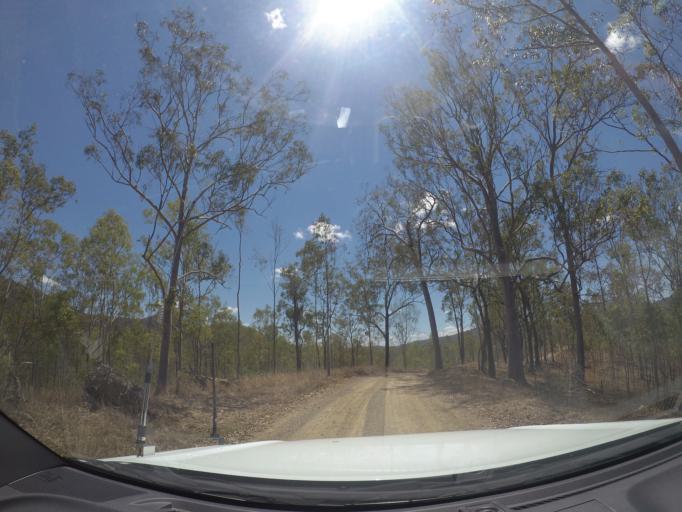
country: AU
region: Queensland
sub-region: Ipswich
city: Springfield Lakes
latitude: -27.8258
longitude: 152.8370
